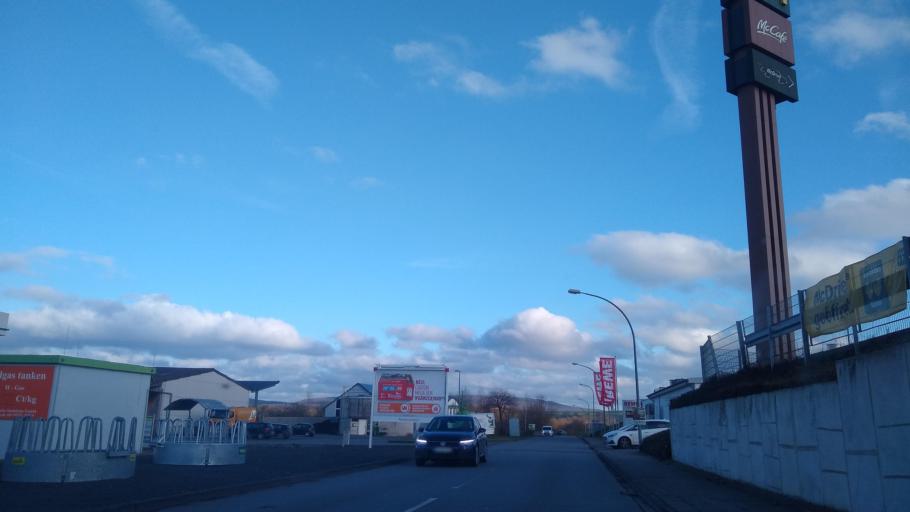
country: DE
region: North Rhine-Westphalia
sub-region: Regierungsbezirk Detmold
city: Steinheim
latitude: 51.8782
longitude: 9.0873
